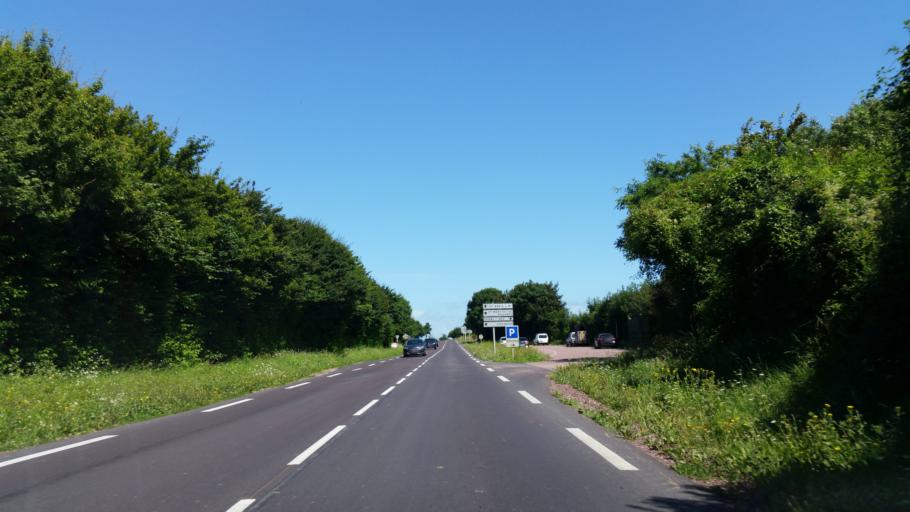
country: FR
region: Lower Normandy
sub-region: Departement de la Manche
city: Carentan
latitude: 49.3329
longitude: -1.2650
